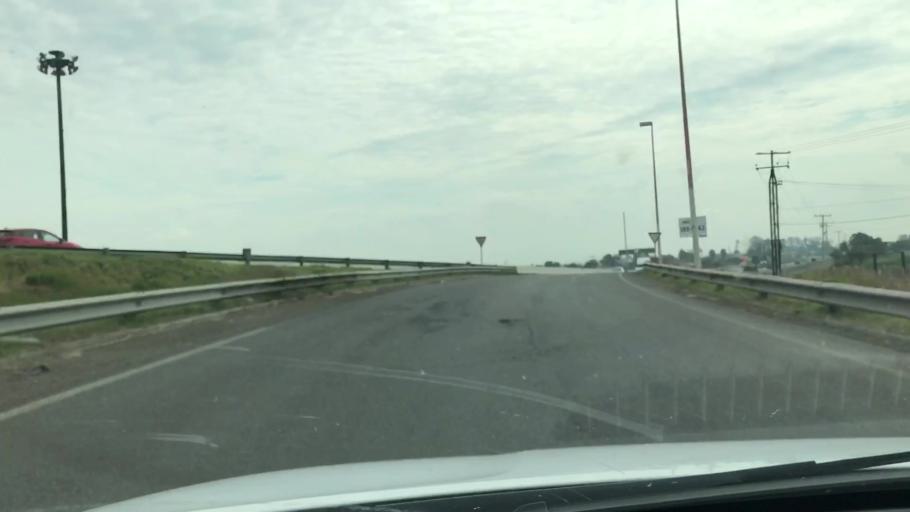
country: MX
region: Guanajuato
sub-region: Irapuato
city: Las Huertas Tercera Seccion
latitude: 20.6494
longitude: -101.3733
